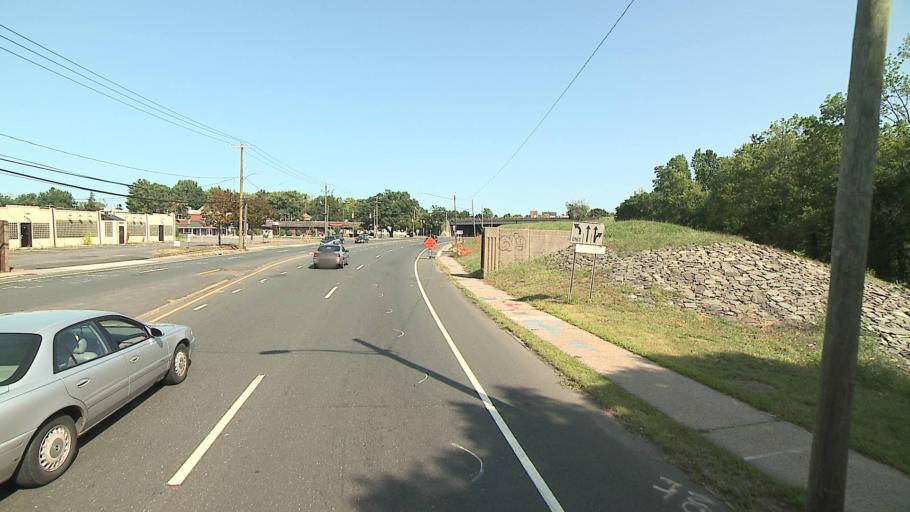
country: US
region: Connecticut
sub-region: Hartford County
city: Hartford
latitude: 41.7627
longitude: -72.6461
